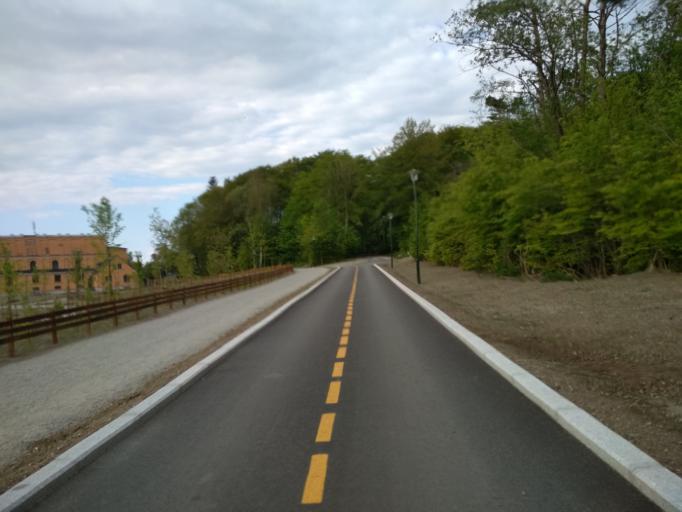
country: NO
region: Rogaland
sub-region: Stavanger
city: Stavanger
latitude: 58.9563
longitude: 5.7233
